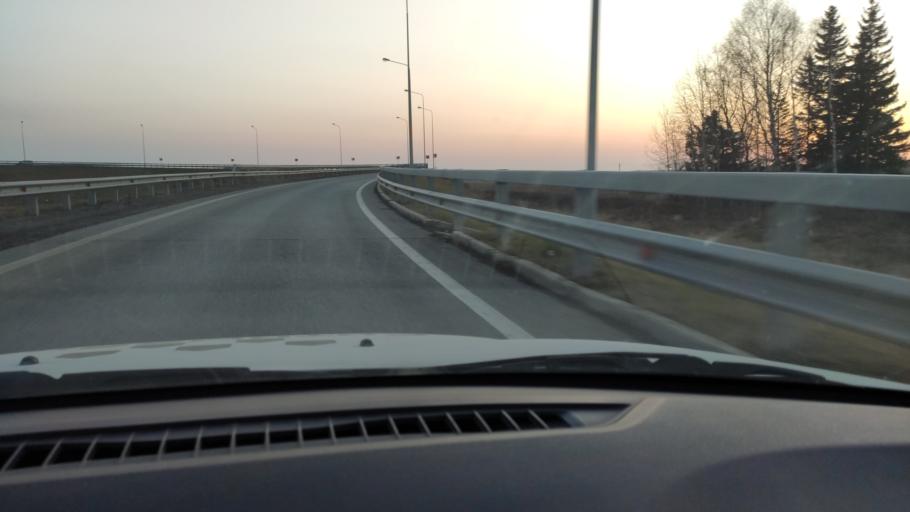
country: RU
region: Perm
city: Zvezdnyy
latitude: 57.7836
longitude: 56.3400
